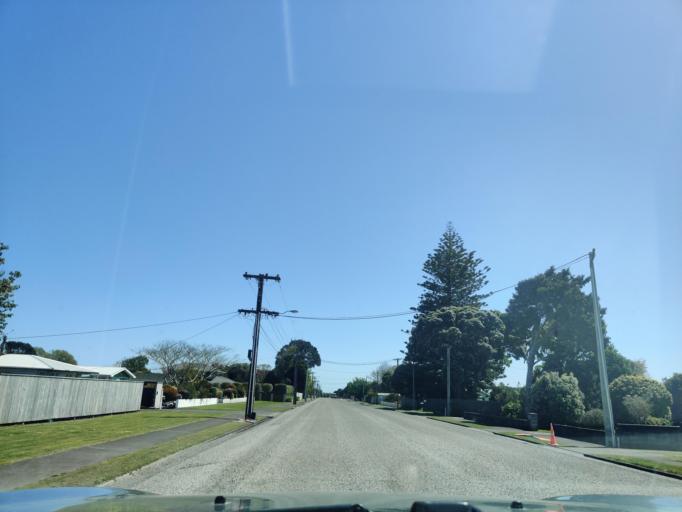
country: NZ
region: Taranaki
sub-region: South Taranaki District
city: Hawera
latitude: -39.5913
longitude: 174.2692
